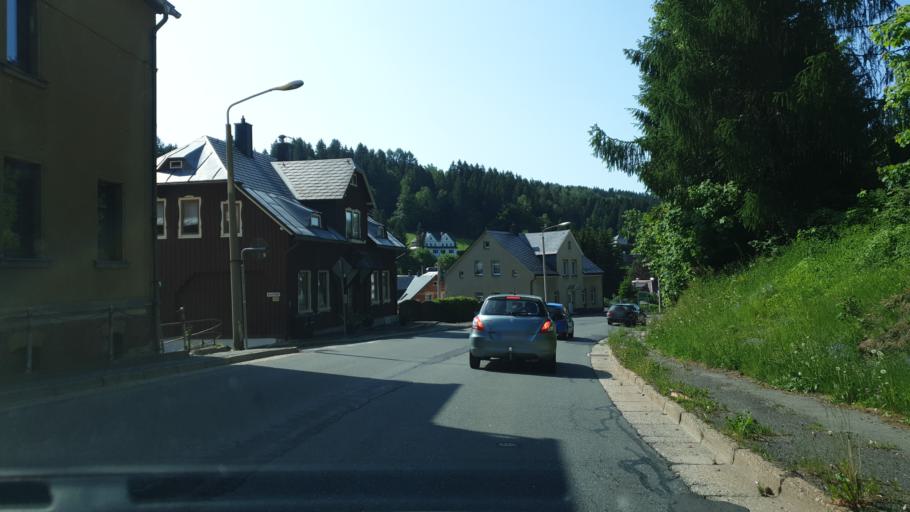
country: DE
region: Saxony
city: Klingenthal
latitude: 50.3834
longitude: 12.4838
